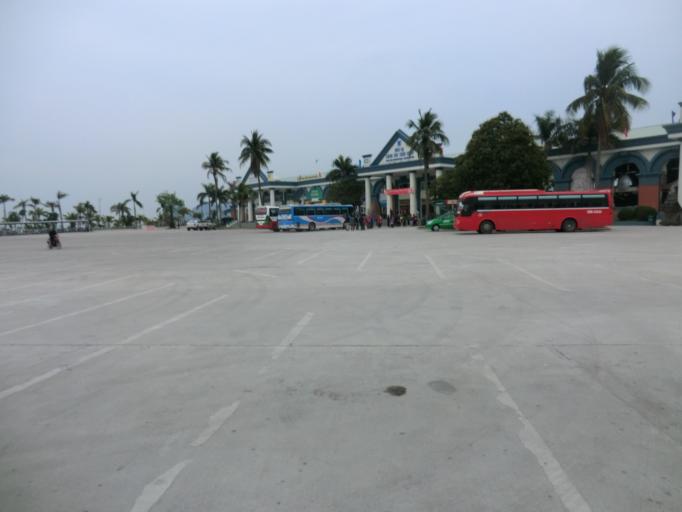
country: VN
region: Quang Ninh
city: Thanh Pho Ha Long
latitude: 20.9233
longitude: 106.9901
